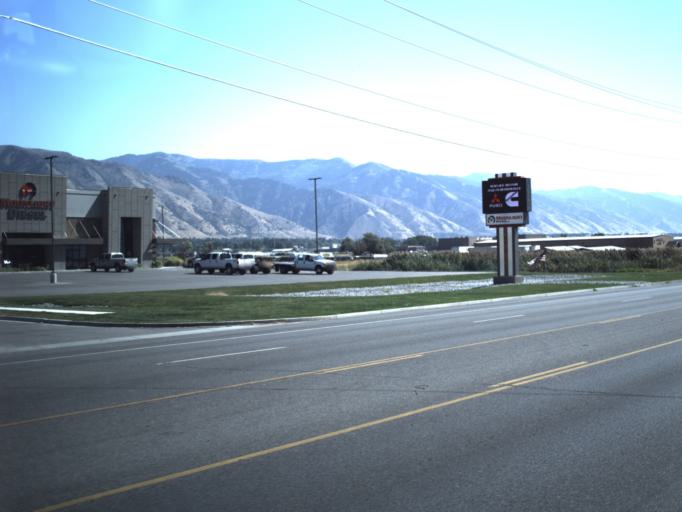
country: US
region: Utah
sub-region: Cache County
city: Hyde Park
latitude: 41.7932
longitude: -111.8337
